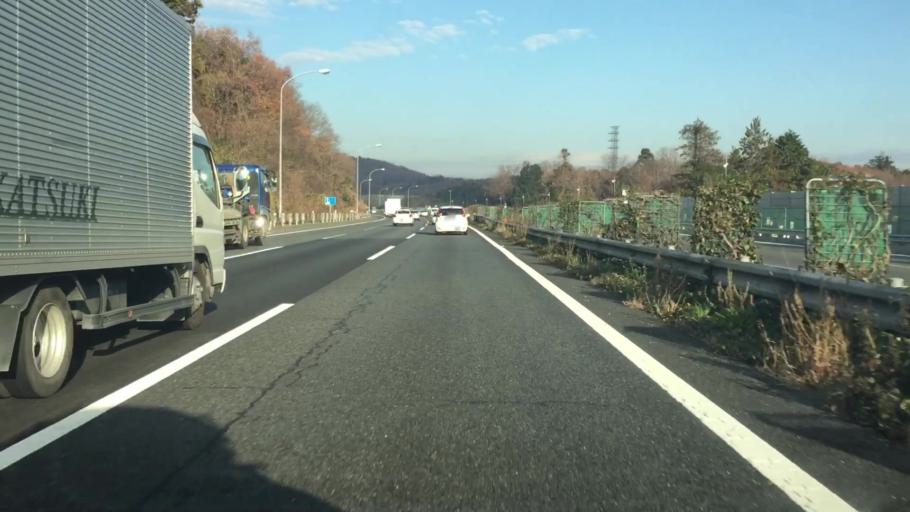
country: JP
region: Saitama
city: Ogawa
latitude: 36.0788
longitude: 139.2997
